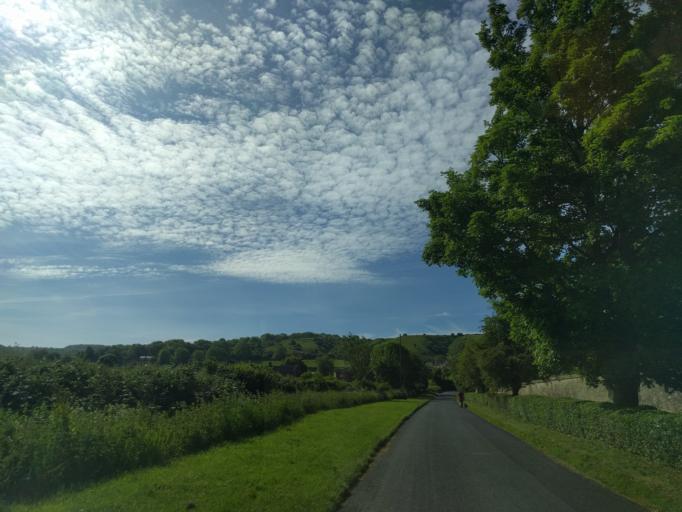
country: GB
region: England
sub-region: Wiltshire
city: Edington
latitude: 51.2808
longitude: -2.1057
